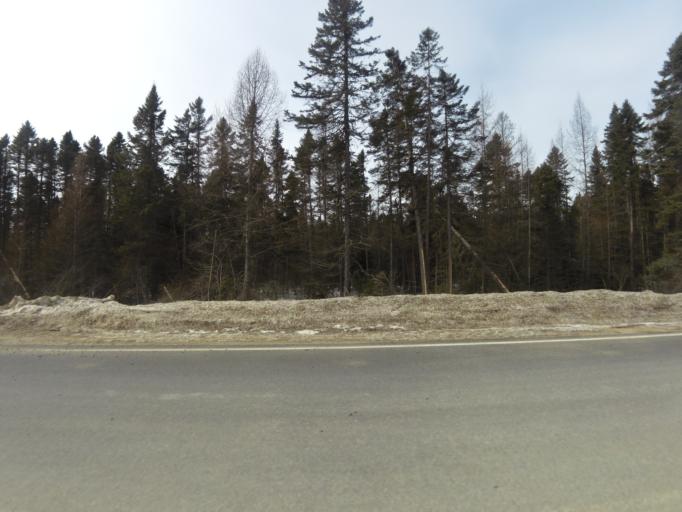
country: CA
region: Quebec
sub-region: Outaouais
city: Val-des-Monts
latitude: 45.9814
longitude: -75.5409
